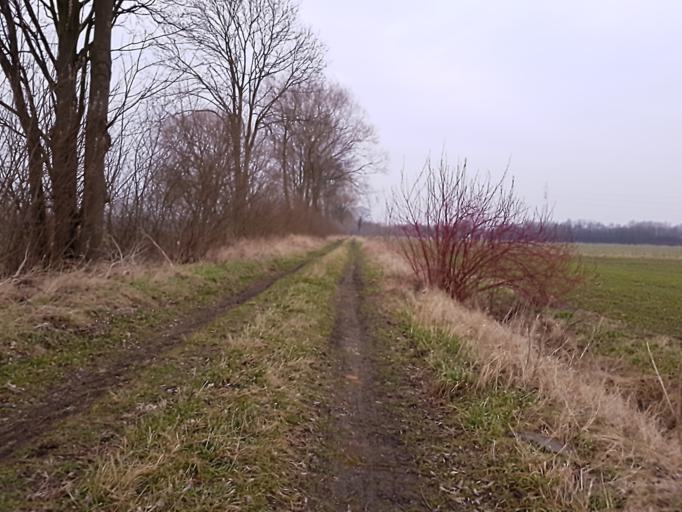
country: BE
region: Flanders
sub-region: Provincie Antwerpen
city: Stabroek
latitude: 51.3391
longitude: 4.3414
